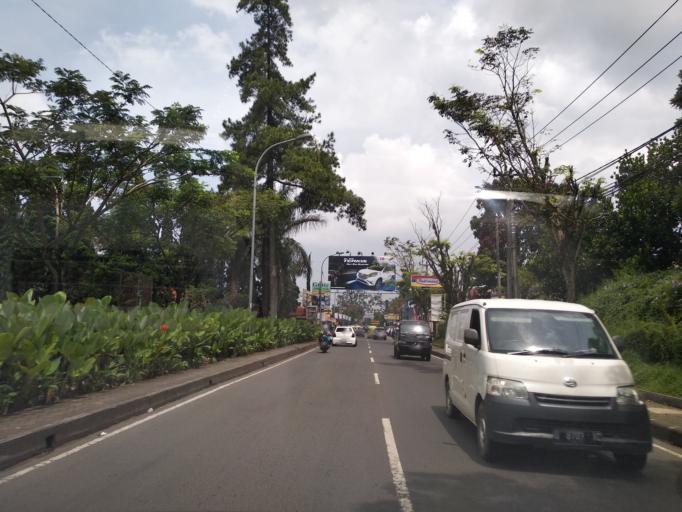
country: ID
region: West Java
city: Lembang
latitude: -6.8156
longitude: 107.6138
